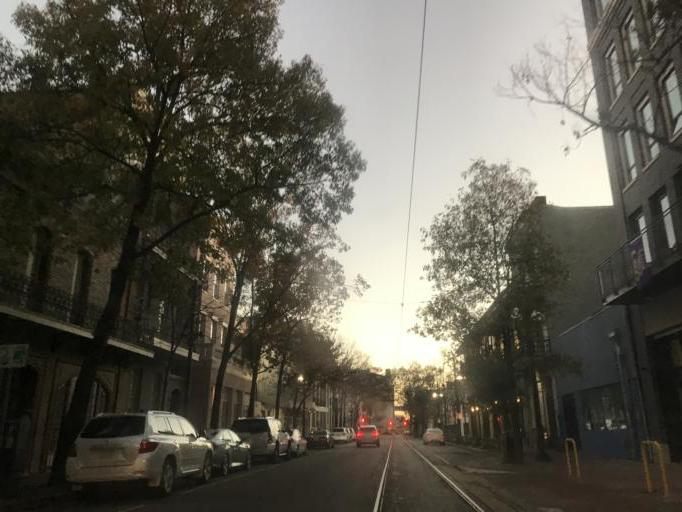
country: US
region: Louisiana
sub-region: Orleans Parish
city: New Orleans
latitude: 29.9457
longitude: -90.0718
